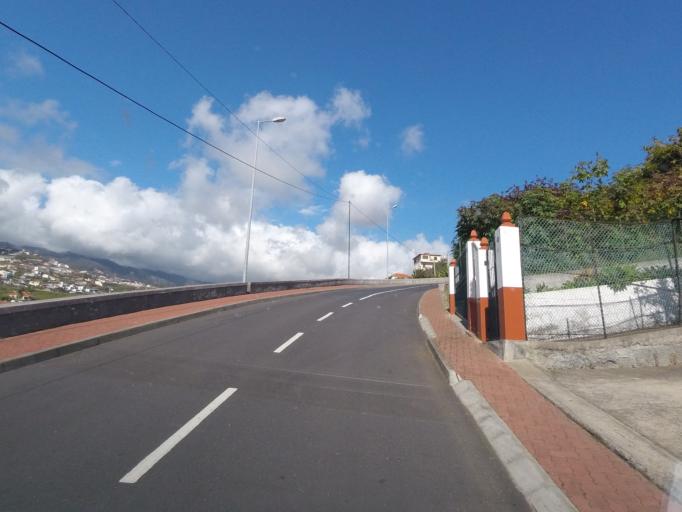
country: PT
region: Madeira
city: Camara de Lobos
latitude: 32.6530
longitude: -16.9768
